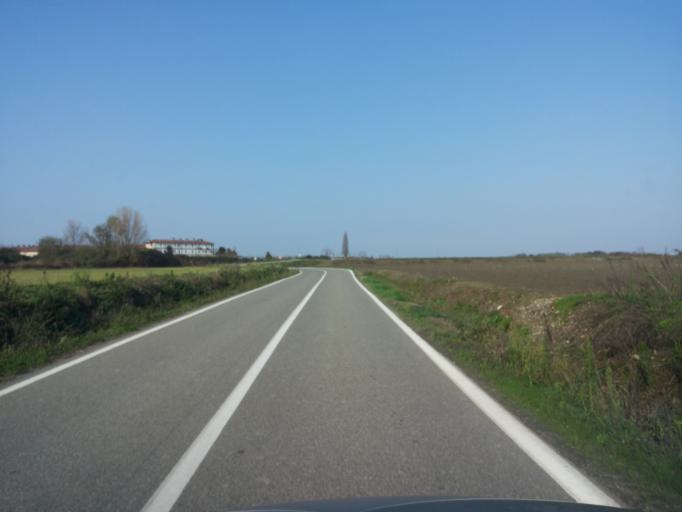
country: IT
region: Piedmont
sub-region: Provincia di Vercelli
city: Caresana
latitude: 45.2307
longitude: 8.4955
